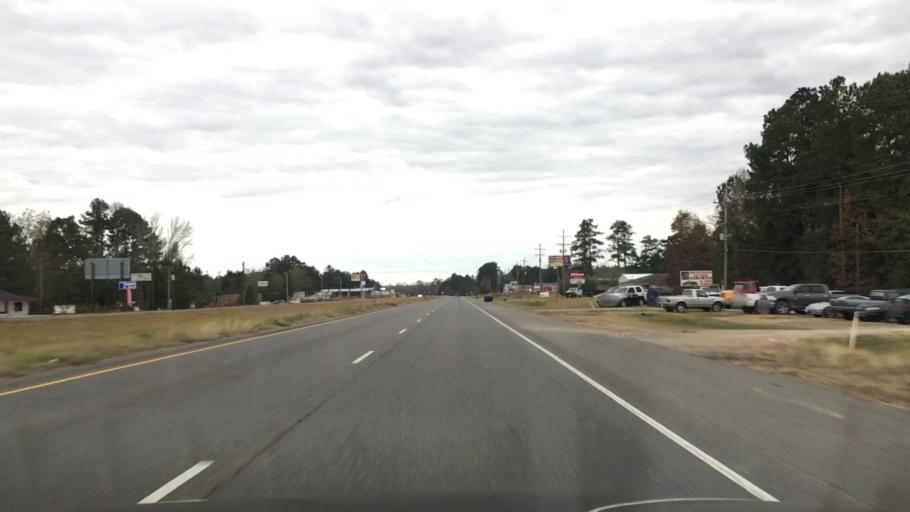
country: US
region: Louisiana
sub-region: Vernon Parish
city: New Llano
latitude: 31.0778
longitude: -93.2730
